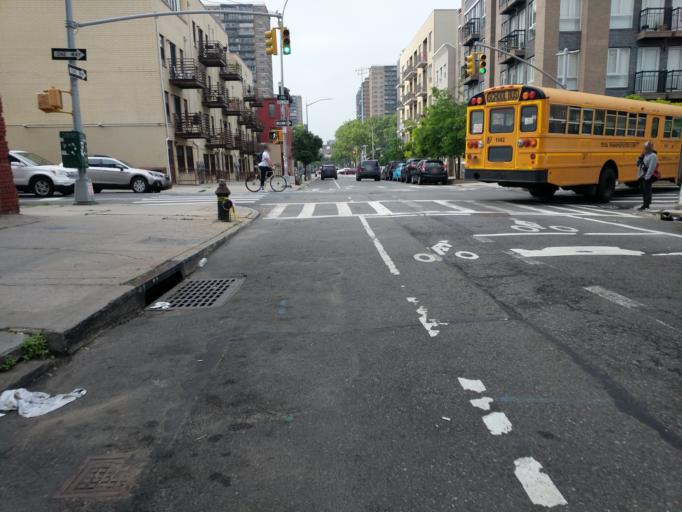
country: US
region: New York
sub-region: Queens County
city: Long Island City
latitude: 40.7079
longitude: -73.9467
